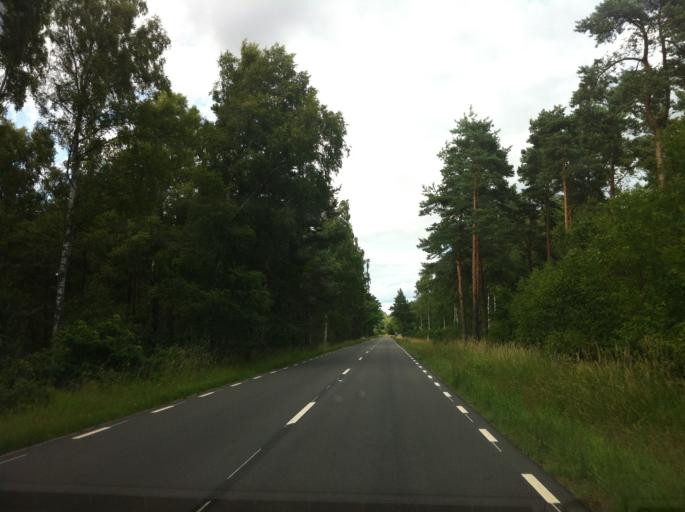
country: SE
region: Skane
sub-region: Ystads Kommun
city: Kopingebro
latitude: 55.3952
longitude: 14.1596
